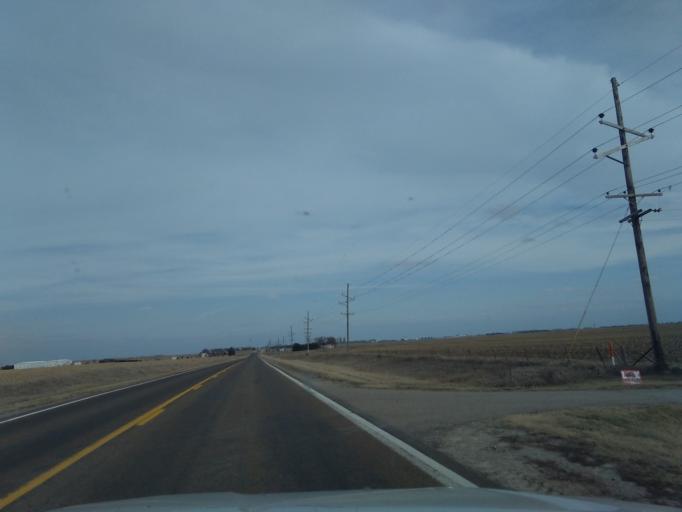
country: US
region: Nebraska
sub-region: Saline County
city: Wilber
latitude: 40.3061
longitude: -97.0389
